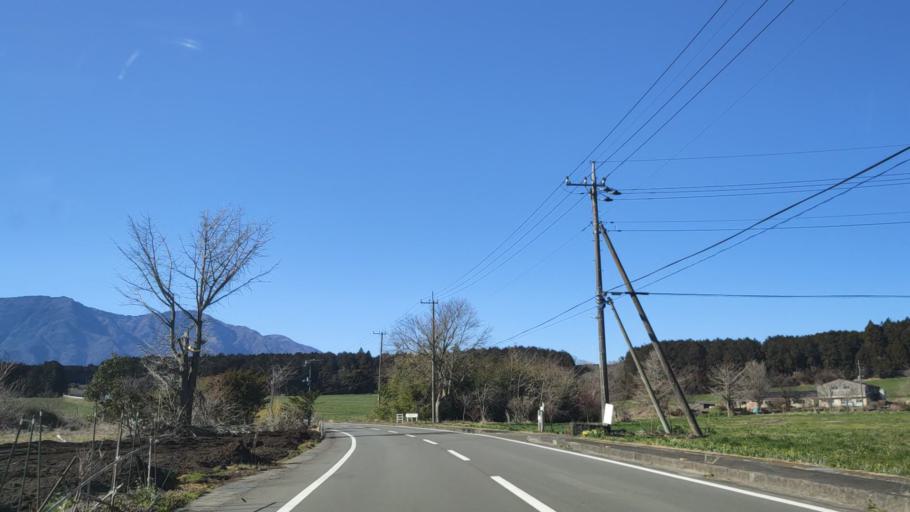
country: JP
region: Yamanashi
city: Fujikawaguchiko
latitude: 35.3659
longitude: 138.6052
